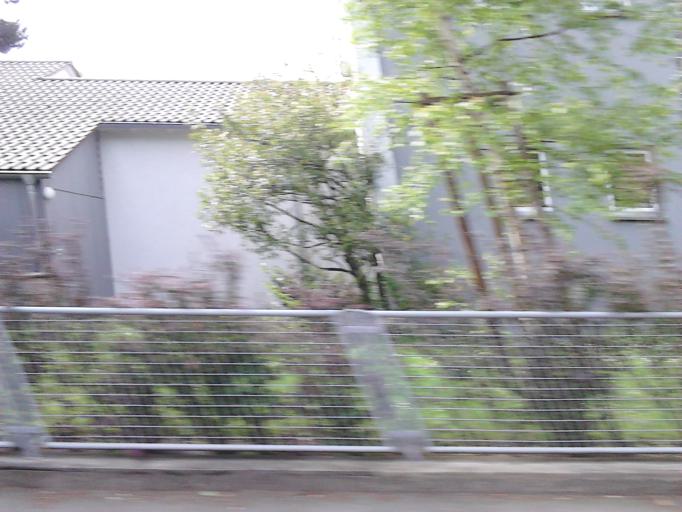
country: DE
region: Baden-Wuerttemberg
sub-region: Tuebingen Region
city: Friedrichshafen
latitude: 47.6532
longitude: 9.4645
